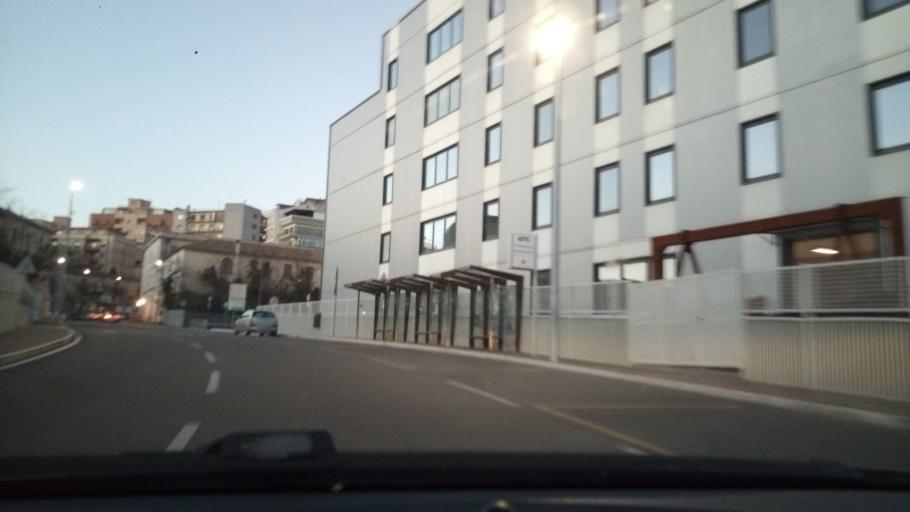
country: IT
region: Calabria
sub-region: Provincia di Catanzaro
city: Siano
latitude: 38.9115
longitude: 16.5885
